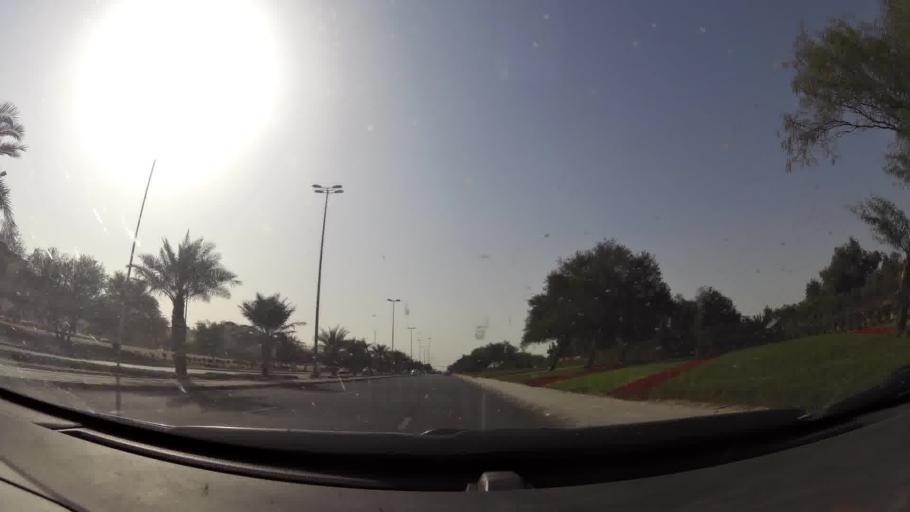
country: KW
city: Bayan
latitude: 29.2820
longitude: 48.0404
